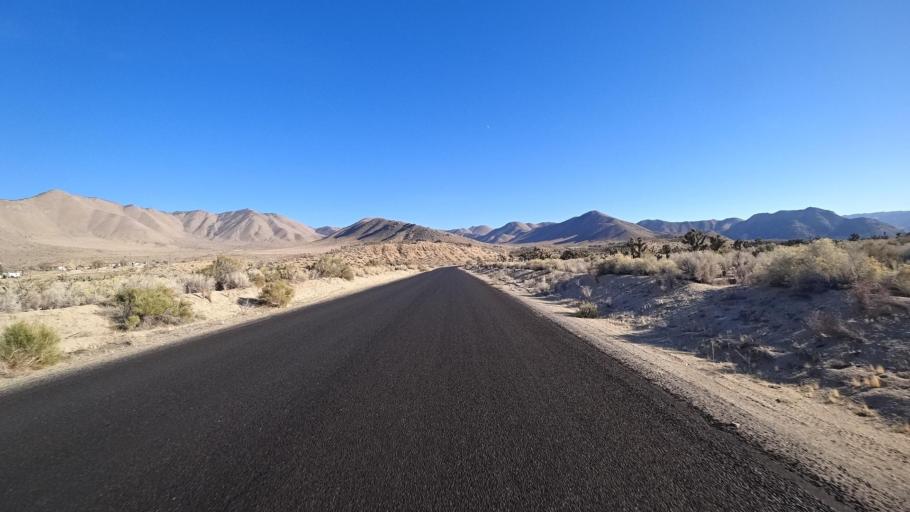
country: US
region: California
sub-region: Kern County
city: Weldon
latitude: 35.6128
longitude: -118.2453
